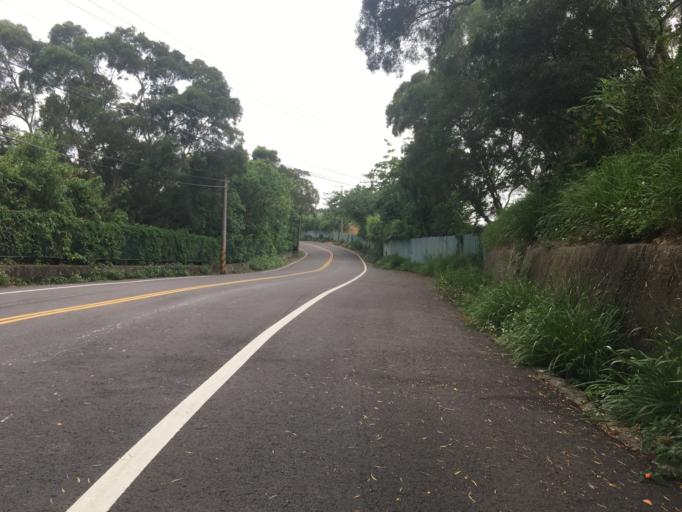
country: TW
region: Taiwan
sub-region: Hsinchu
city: Hsinchu
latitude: 24.7432
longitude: 120.9830
